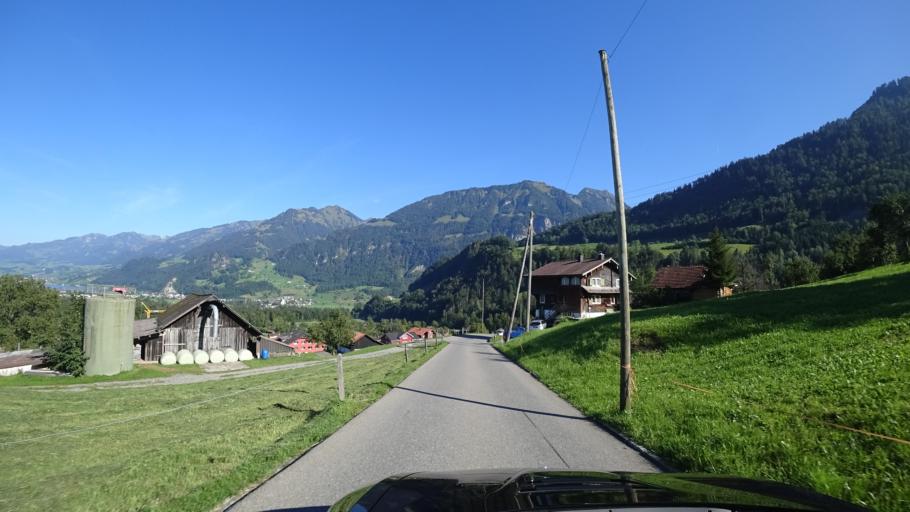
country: CH
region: Obwalden
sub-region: Obwalden
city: Giswil
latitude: 46.8318
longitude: 8.1521
